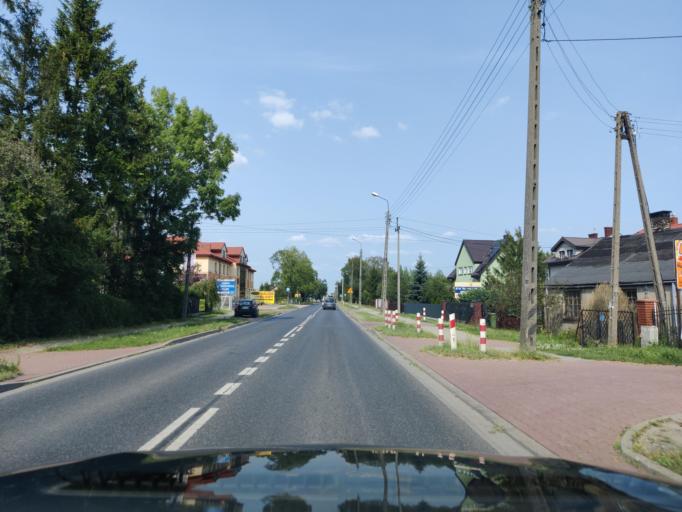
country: PL
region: Masovian Voivodeship
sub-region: Powiat pultuski
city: Pultusk
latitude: 52.7206
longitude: 21.0859
